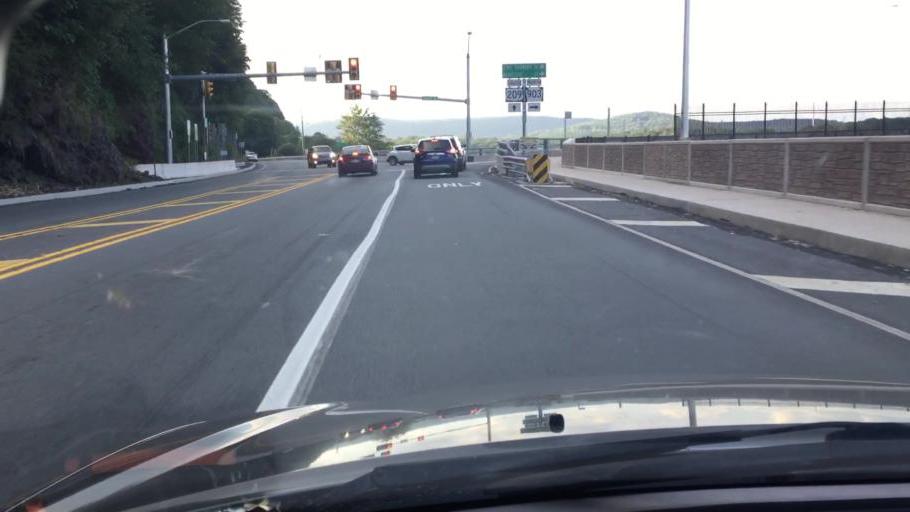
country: US
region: Pennsylvania
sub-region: Carbon County
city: Jim Thorpe
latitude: 40.8683
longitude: -75.7383
